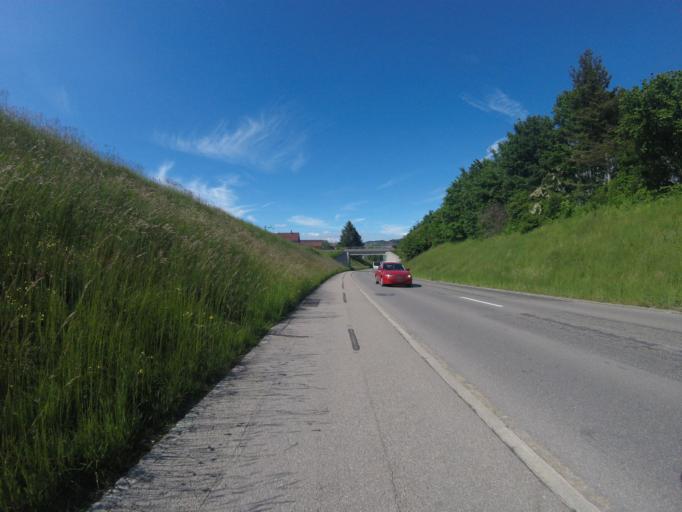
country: CH
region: Saint Gallen
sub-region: Wahlkreis Wil
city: Wil
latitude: 47.4432
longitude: 9.0501
